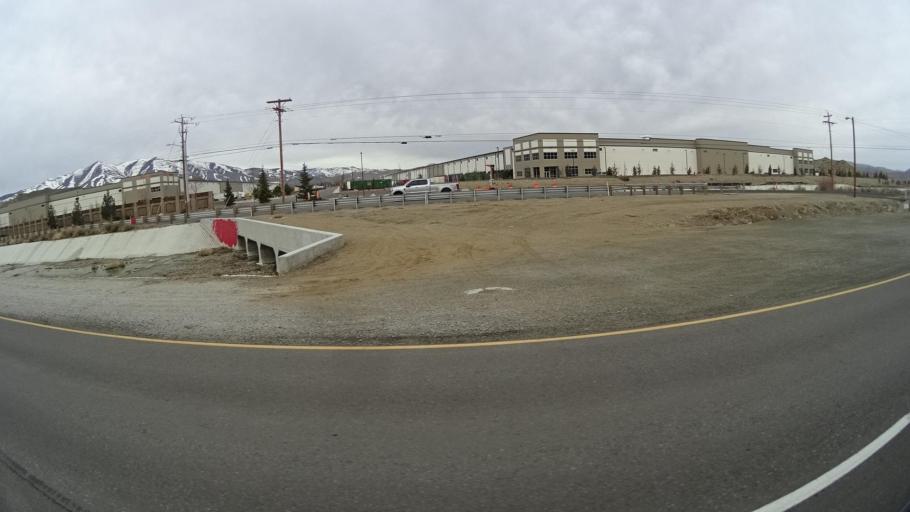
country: US
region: Nevada
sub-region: Washoe County
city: Lemmon Valley
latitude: 39.6318
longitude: -119.8451
